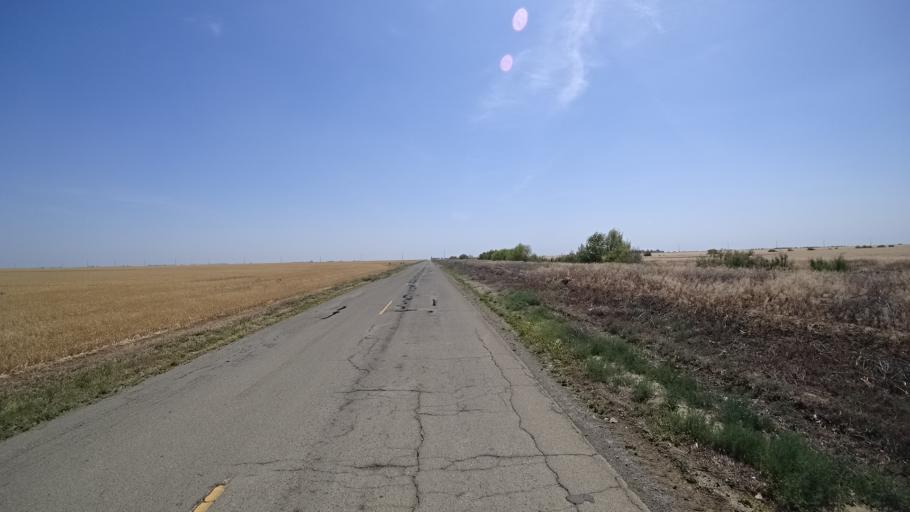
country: US
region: California
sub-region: Kings County
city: Stratford
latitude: 36.1378
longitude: -119.9163
